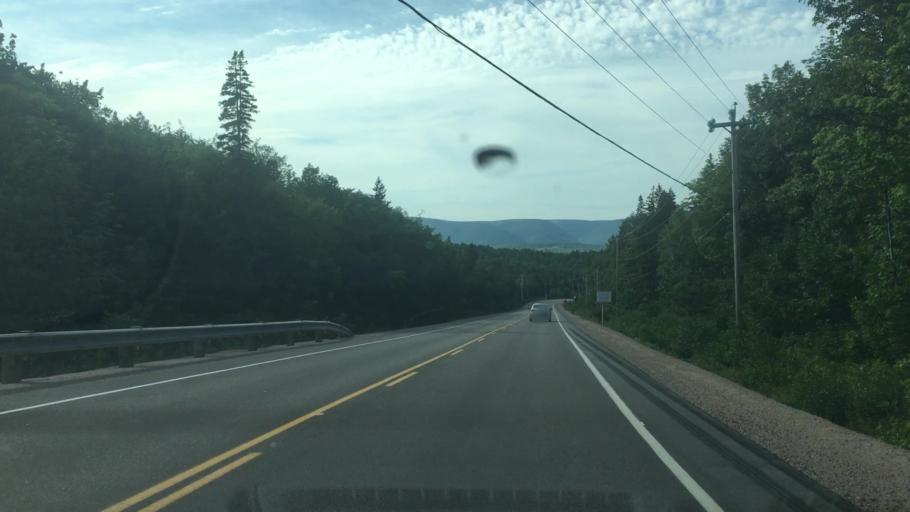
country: CA
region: Nova Scotia
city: Sydney Mines
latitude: 46.8559
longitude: -60.4580
